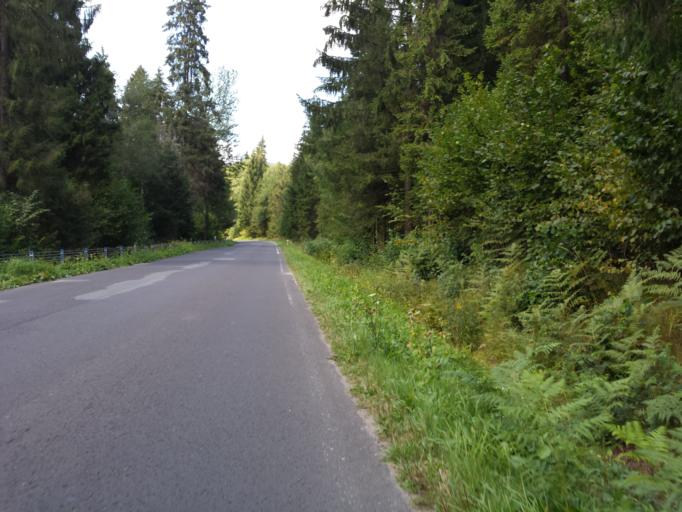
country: PL
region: Subcarpathian Voivodeship
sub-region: Powiat leski
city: Cisna
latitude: 49.1875
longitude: 22.4132
